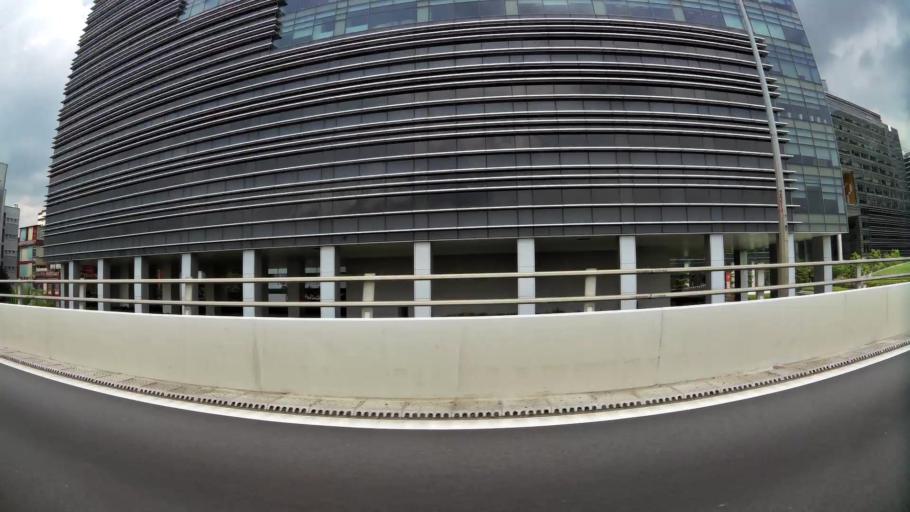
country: SG
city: Singapore
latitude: 1.2744
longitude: 103.7977
